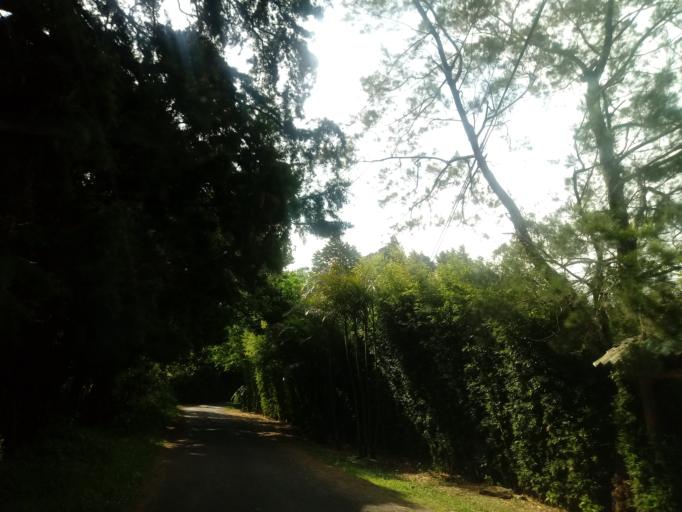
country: CR
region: Heredia
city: Angeles
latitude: 10.0390
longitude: -84.0410
